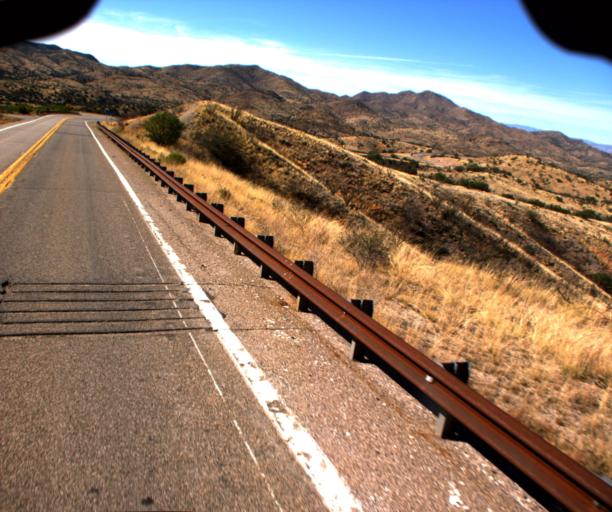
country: US
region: Arizona
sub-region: Pima County
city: Corona de Tucson
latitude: 31.8222
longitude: -110.7126
